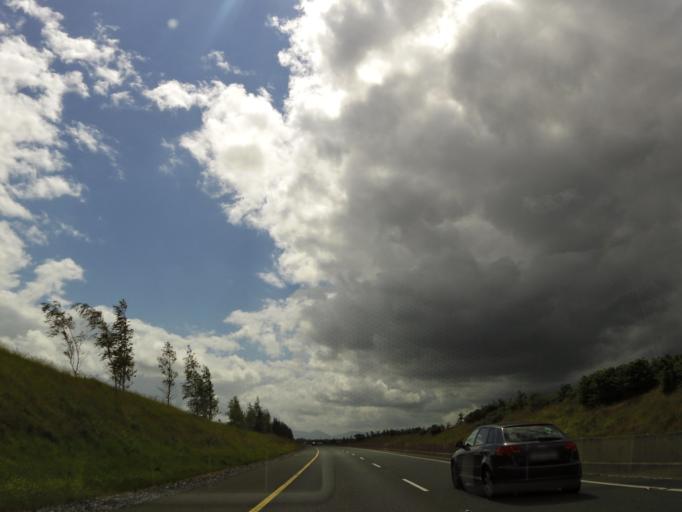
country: IE
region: Munster
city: Cashel
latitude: 52.4783
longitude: -7.9066
